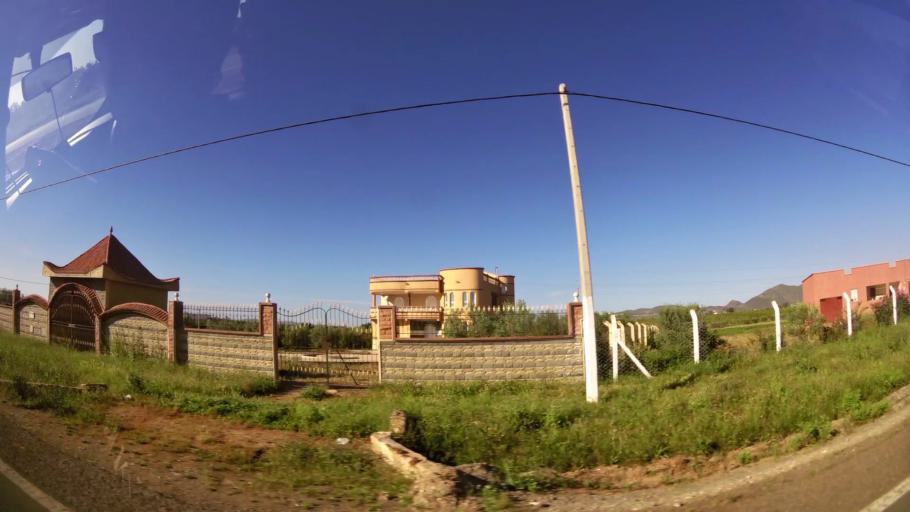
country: MA
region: Oriental
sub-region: Berkane-Taourirt
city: Ahfir
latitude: 34.9941
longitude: -2.1631
